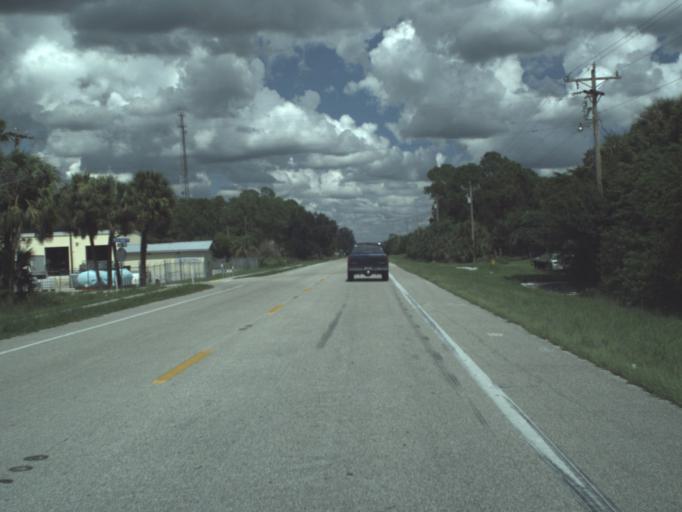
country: US
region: Florida
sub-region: Collier County
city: Immokalee
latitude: 26.5509
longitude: -81.4357
